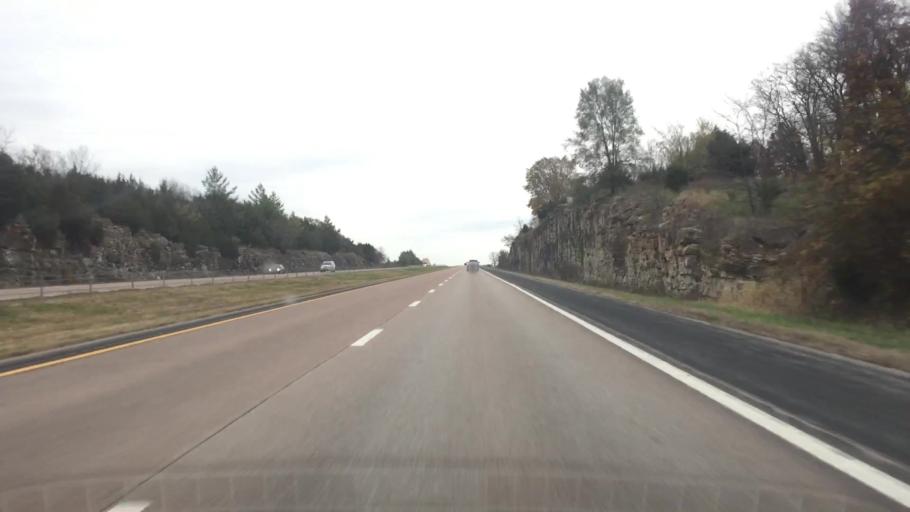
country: US
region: Missouri
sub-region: Boone County
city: Ashland
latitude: 38.7046
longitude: -92.2545
